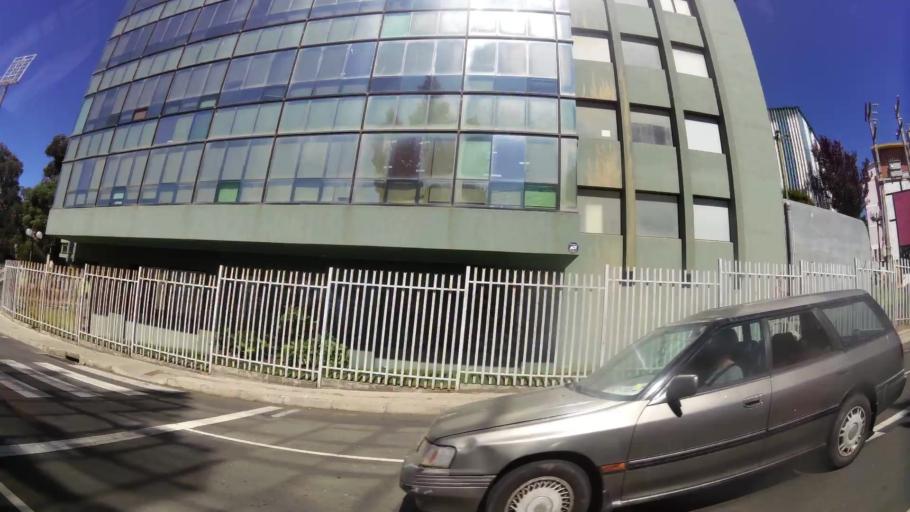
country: CL
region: Valparaiso
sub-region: Provincia de Valparaiso
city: Valparaiso
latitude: -33.0234
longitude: -71.6414
